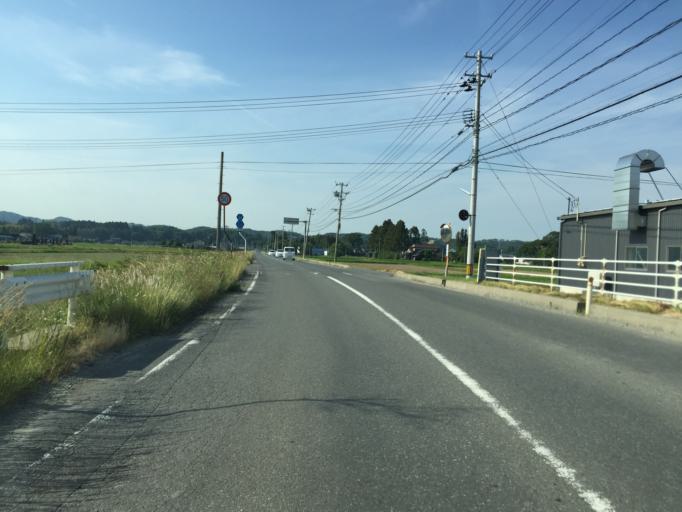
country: JP
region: Fukushima
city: Namie
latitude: 37.6602
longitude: 140.9331
